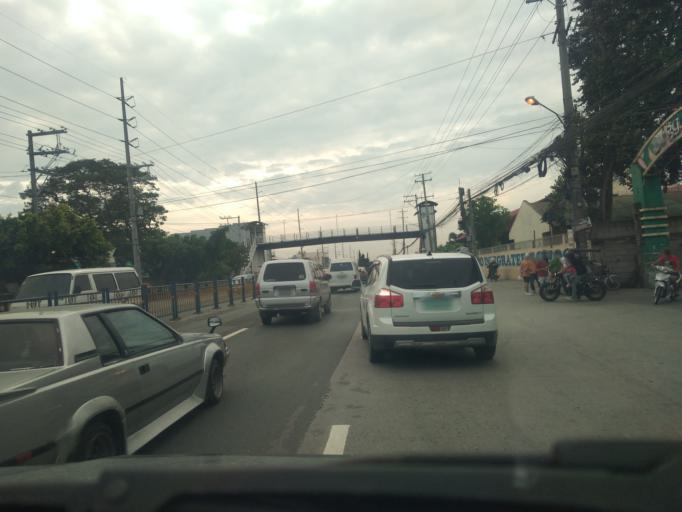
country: PH
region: Central Luzon
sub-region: Province of Pampanga
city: Magliman
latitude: 15.0570
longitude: 120.6587
